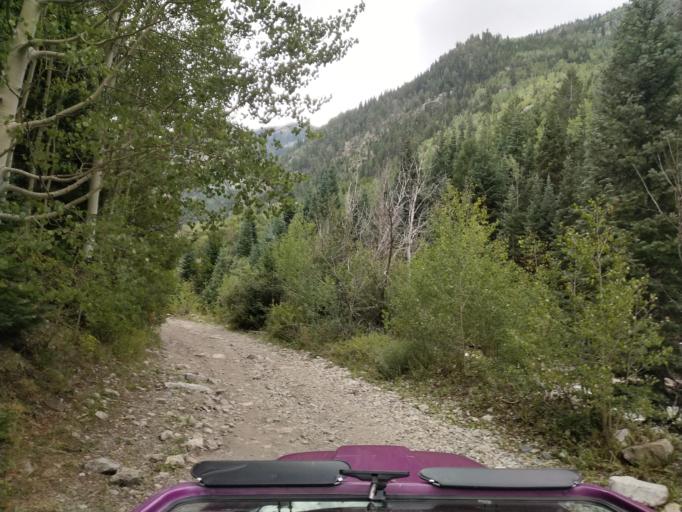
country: US
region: Colorado
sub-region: Gunnison County
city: Crested Butte
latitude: 39.0564
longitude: -107.1338
